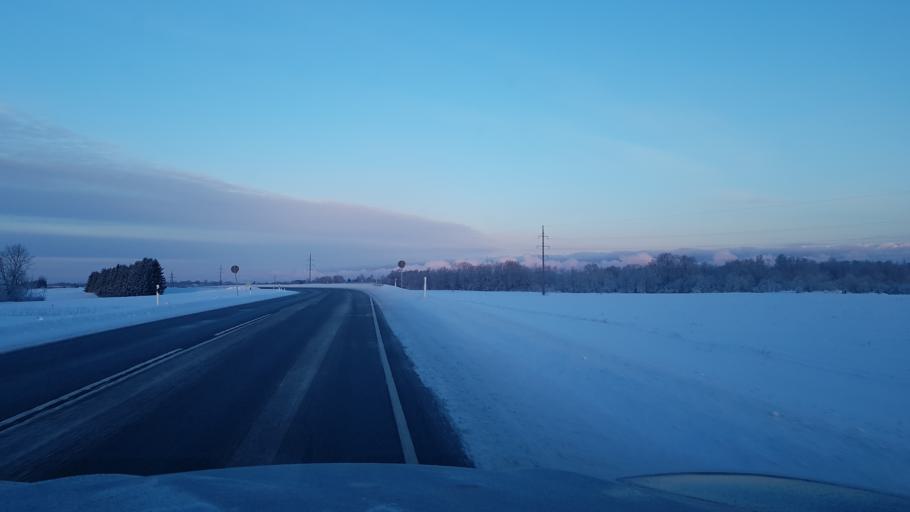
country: EE
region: Ida-Virumaa
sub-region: Narva-Joesuu linn
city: Narva-Joesuu
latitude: 59.4034
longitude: 28.0529
